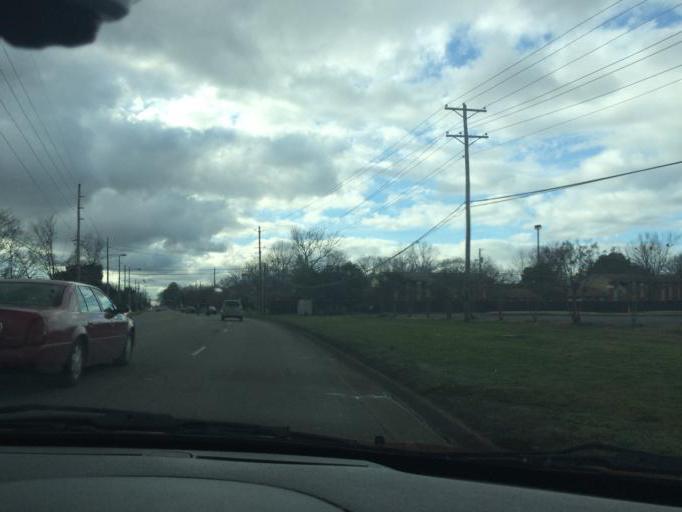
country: US
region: Alabama
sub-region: Madison County
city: Huntsville
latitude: 34.7127
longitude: -86.6139
